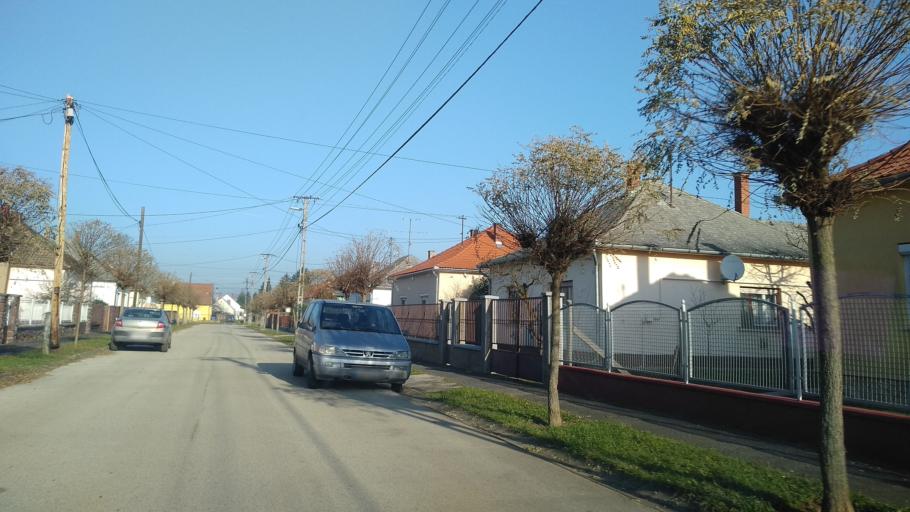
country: HU
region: Somogy
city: Barcs
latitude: 45.9638
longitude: 17.4528
